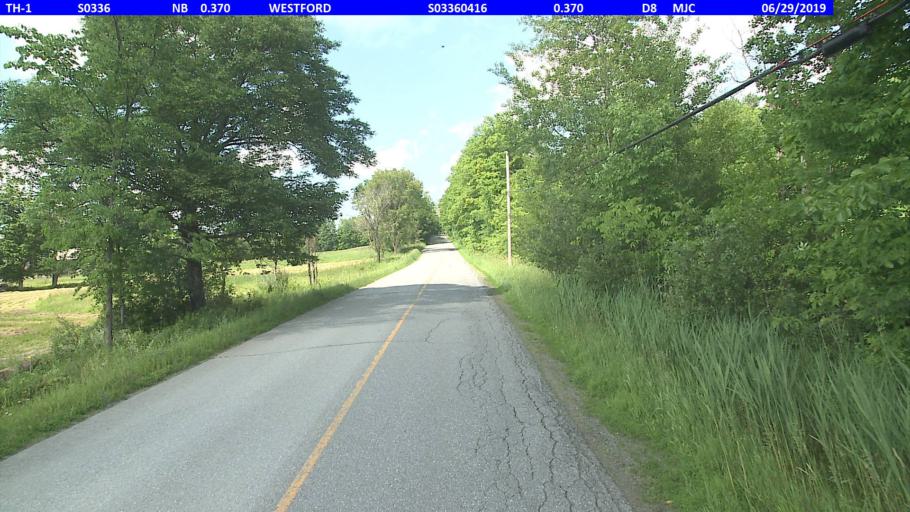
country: US
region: Vermont
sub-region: Chittenden County
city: Milton
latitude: 44.5698
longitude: -73.0597
